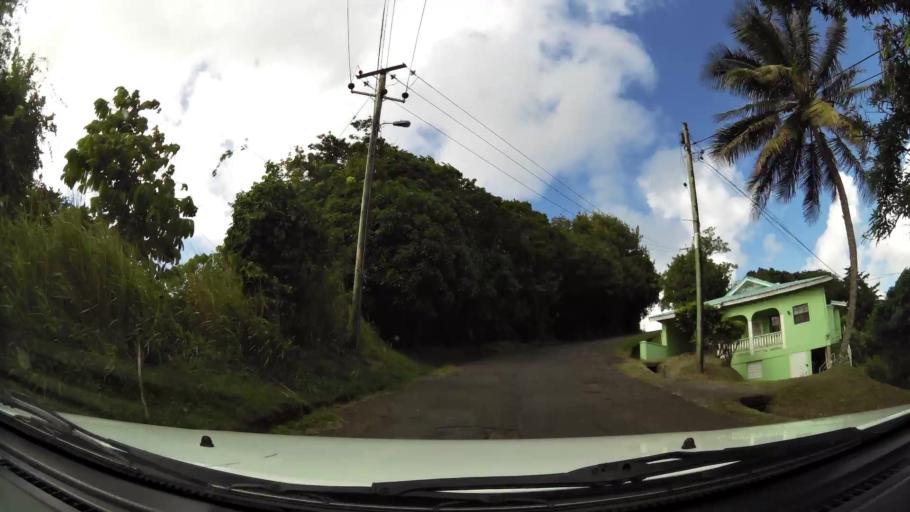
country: LC
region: Castries Quarter
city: Bisee
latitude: 14.0084
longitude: -60.9713
